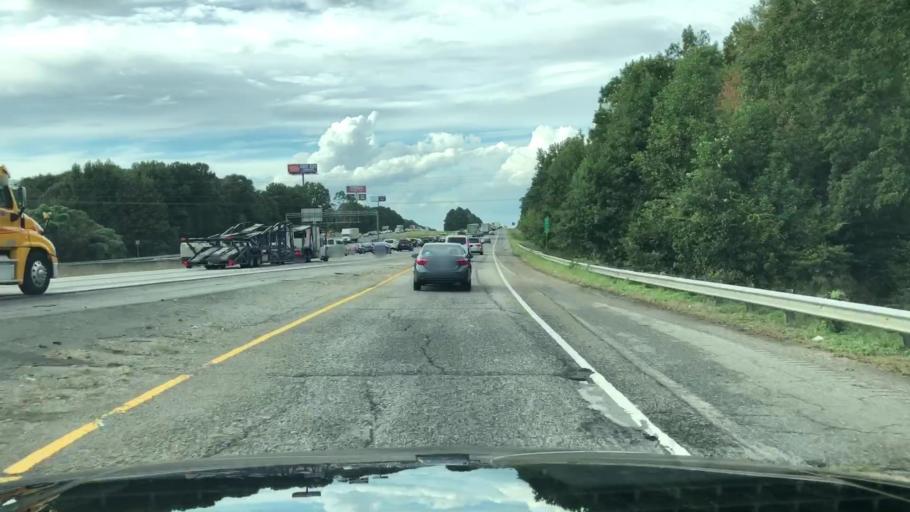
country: US
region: Georgia
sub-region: Henry County
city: Locust Grove
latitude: 33.3549
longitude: -84.1256
